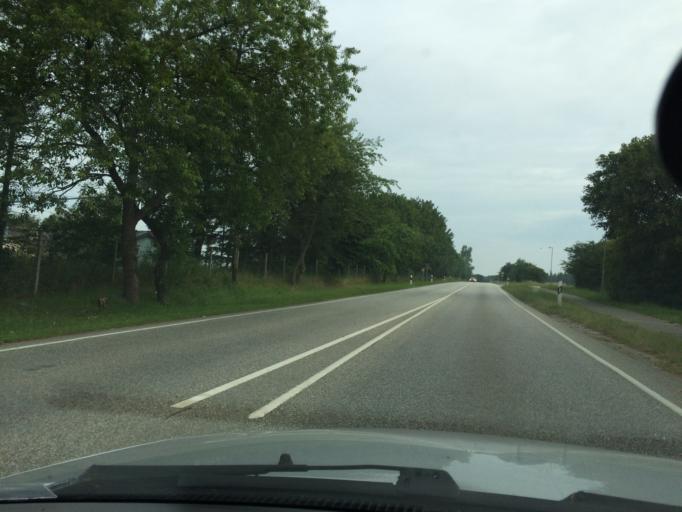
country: DE
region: Schleswig-Holstein
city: Oeversee
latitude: 54.7062
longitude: 9.4382
